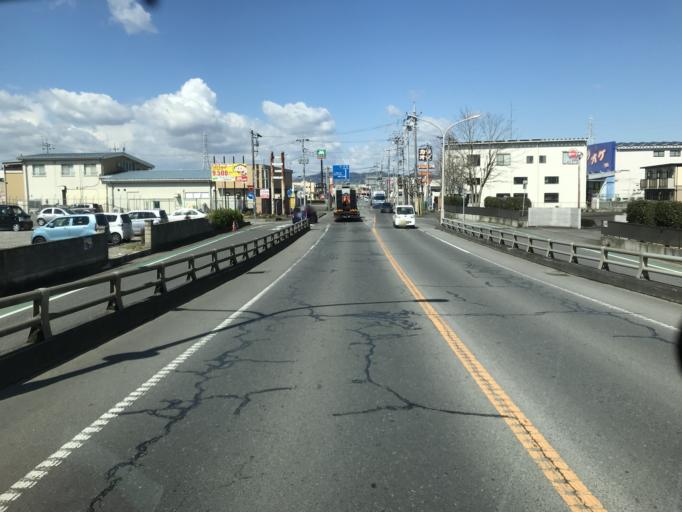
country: JP
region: Ibaraki
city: Ishioka
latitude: 36.1168
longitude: 140.2418
